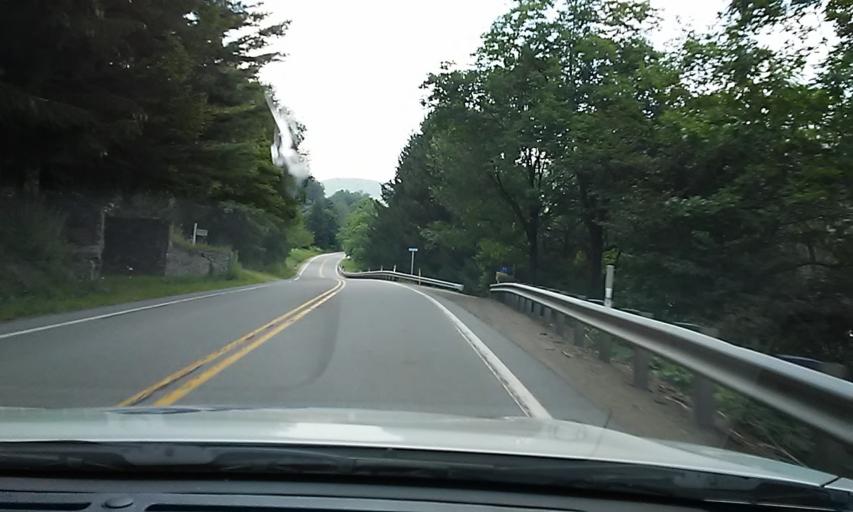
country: US
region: Pennsylvania
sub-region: Potter County
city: Galeton
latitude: 41.8033
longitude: -77.7751
